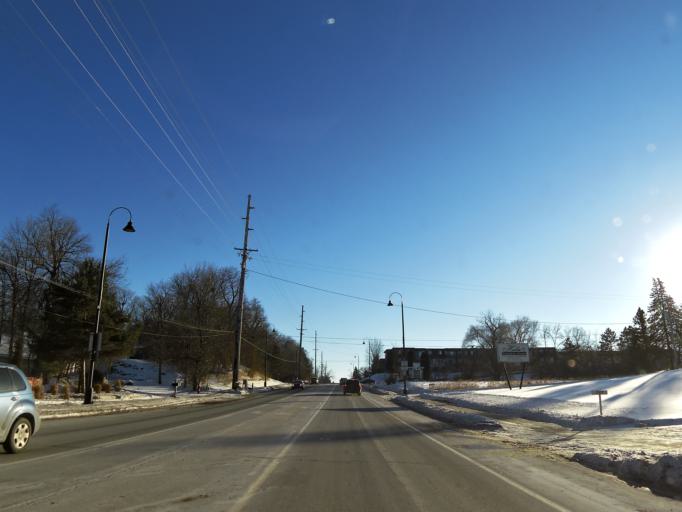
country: US
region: Minnesota
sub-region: Hennepin County
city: Mound
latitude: 44.9461
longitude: -93.6659
